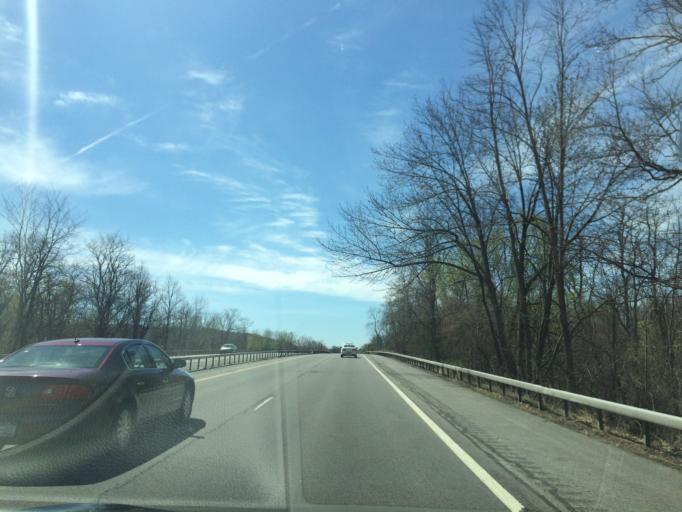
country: US
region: New York
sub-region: Monroe County
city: Fairport
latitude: 43.0663
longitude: -77.4729
